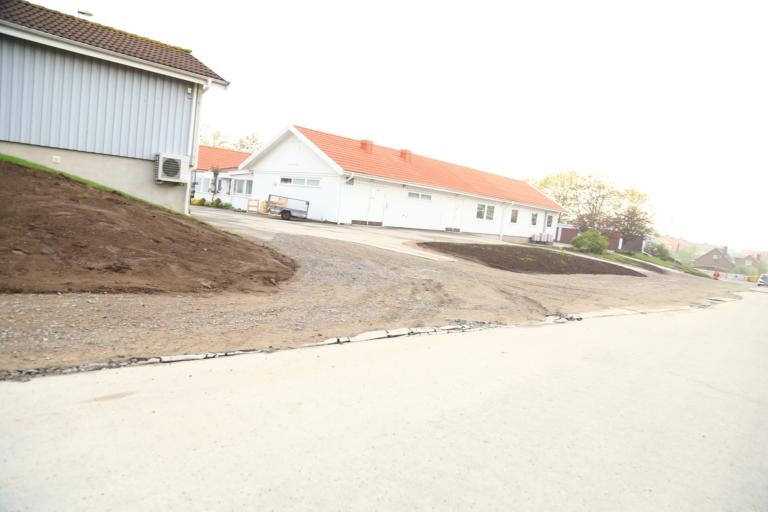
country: SE
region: Halland
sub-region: Varbergs Kommun
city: Varberg
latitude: 57.0943
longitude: 12.2596
